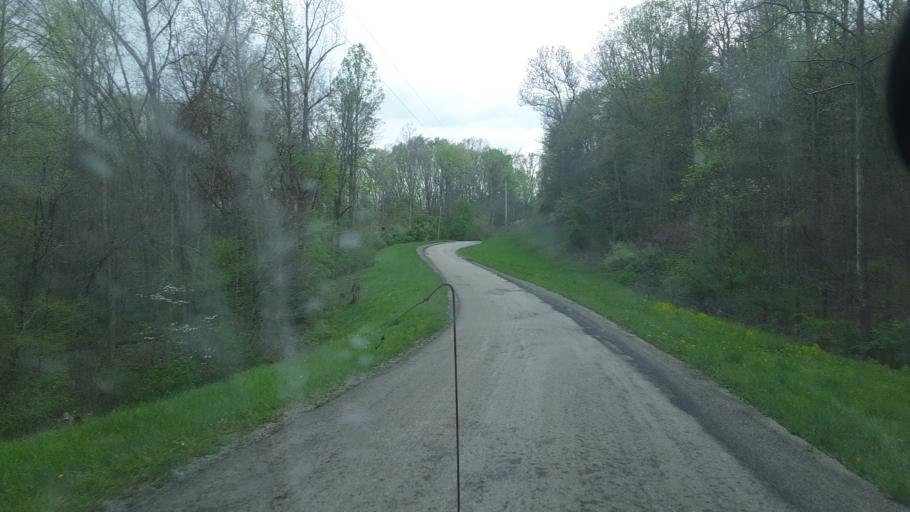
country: US
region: Ohio
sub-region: Noble County
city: Caldwell
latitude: 39.7256
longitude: -81.6783
